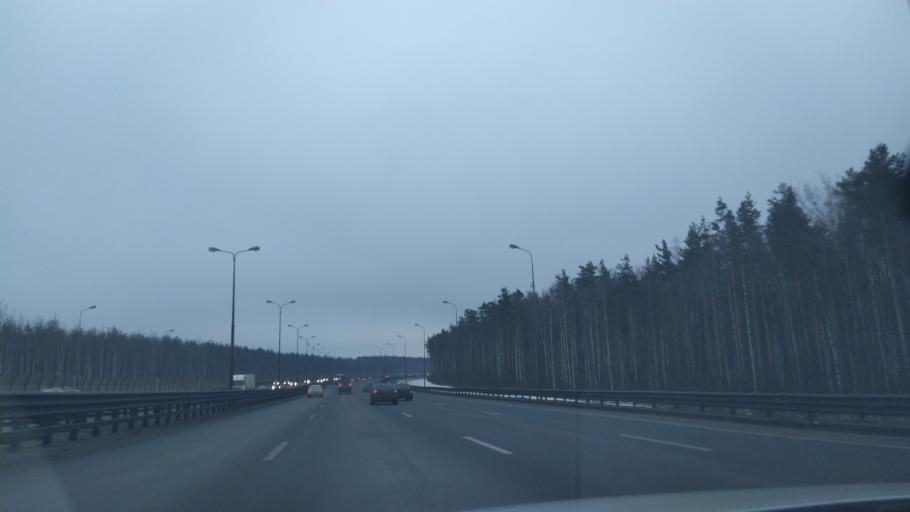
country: RU
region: St.-Petersburg
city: Krasnogvargeisky
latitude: 59.9751
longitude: 30.5382
